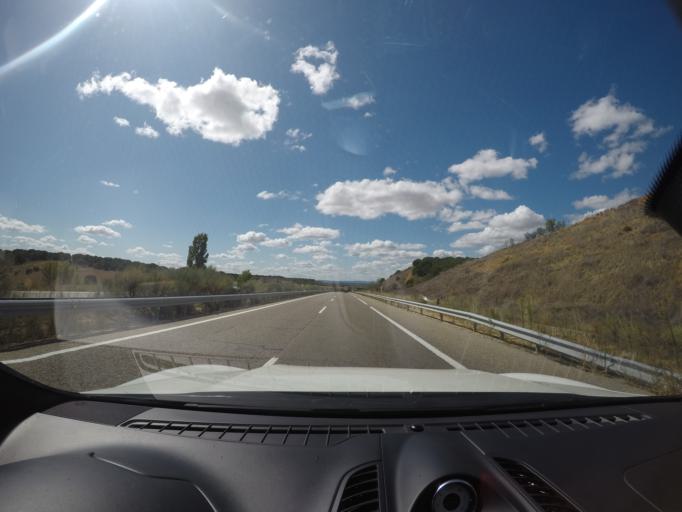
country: ES
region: Castille and Leon
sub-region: Provincia de Zamora
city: Quiruelas de Vidriales
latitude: 42.0289
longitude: -5.7989
